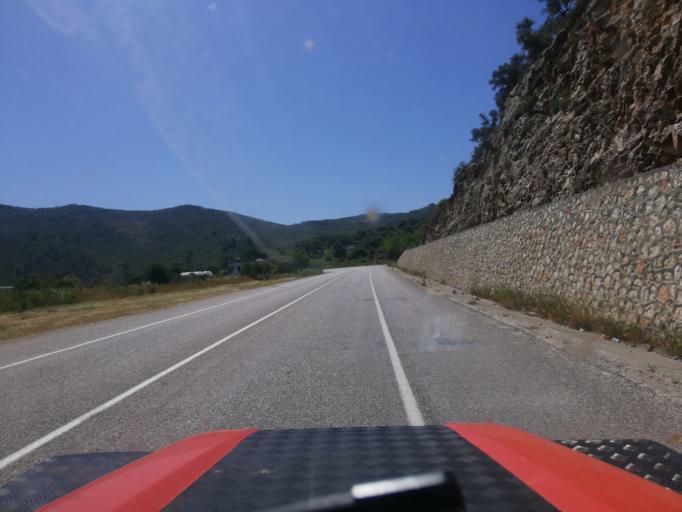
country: TR
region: Antalya
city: Kalkan
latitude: 36.2754
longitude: 29.3619
